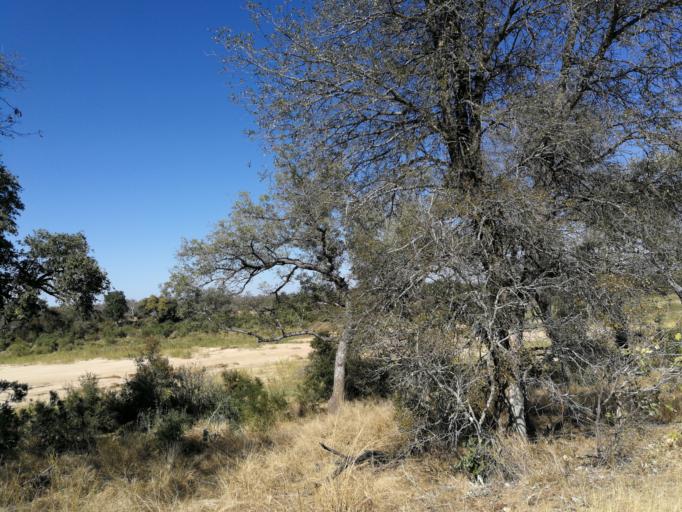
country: ZA
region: Limpopo
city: Thulamahashi
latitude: -24.9541
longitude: 31.6509
